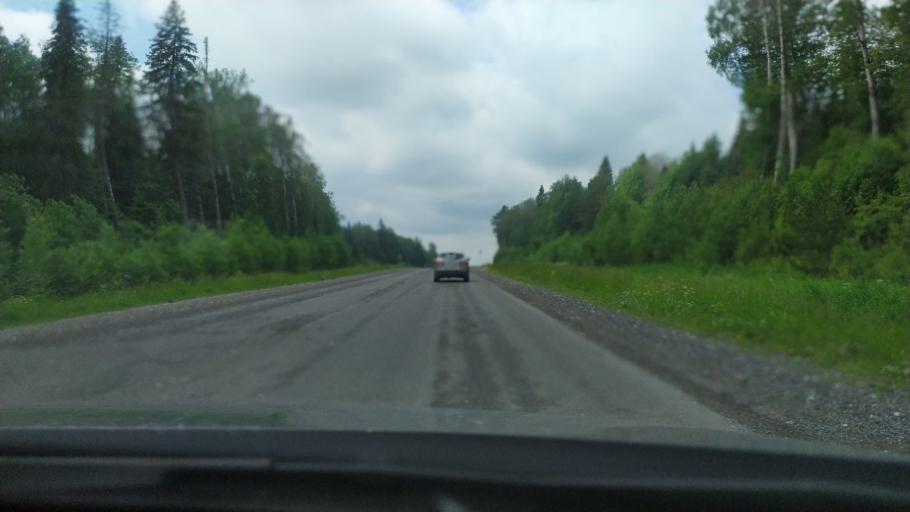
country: RU
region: Perm
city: Kalino
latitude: 58.2702
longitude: 57.3703
